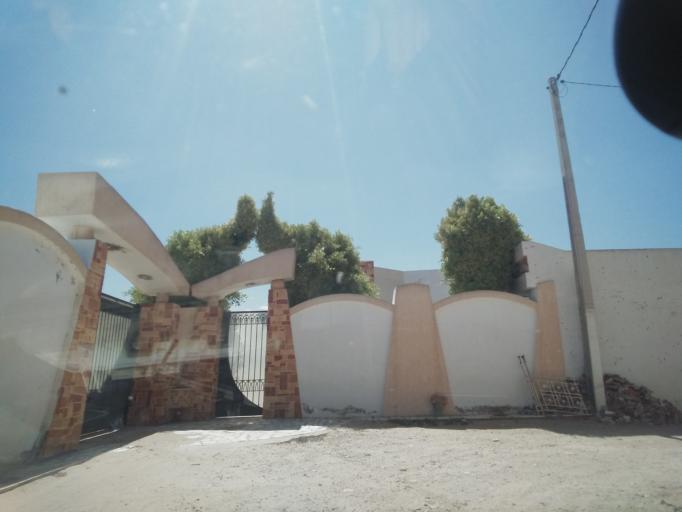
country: TN
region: Safaqis
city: Al Qarmadah
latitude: 34.8251
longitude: 10.7654
